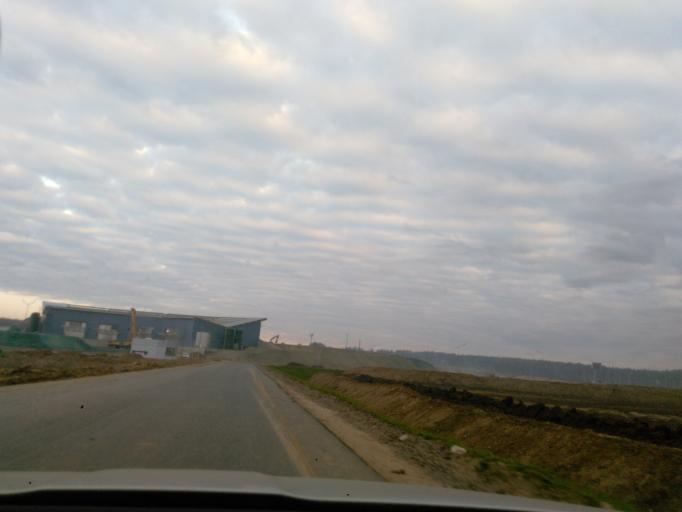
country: RU
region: Moskovskaya
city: Novopodrezkovo
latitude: 55.9600
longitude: 37.3659
